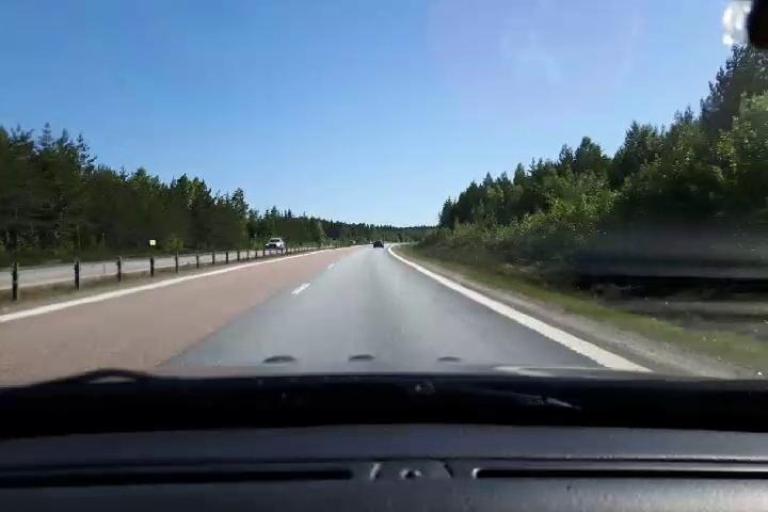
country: SE
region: Gaevleborg
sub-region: Soderhamns Kommun
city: Soderhamn
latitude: 61.4099
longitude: 16.9930
